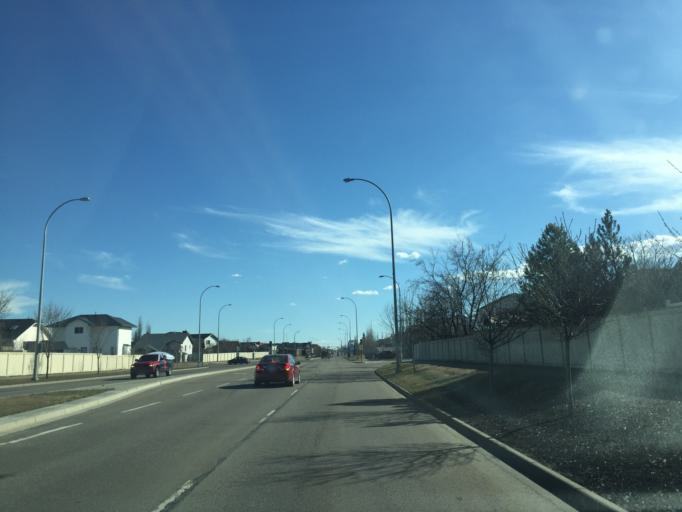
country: CA
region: Alberta
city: Airdrie
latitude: 51.2962
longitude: -114.0254
